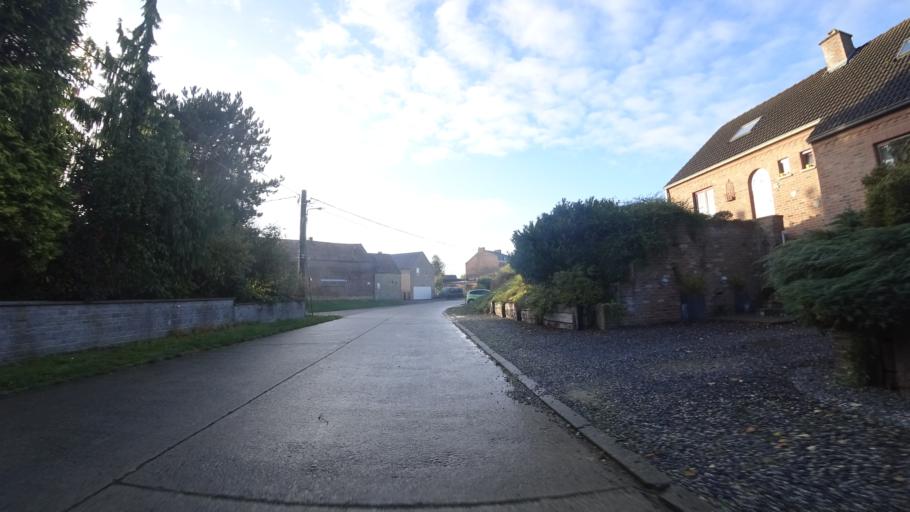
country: BE
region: Wallonia
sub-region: Province de Namur
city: Floreffe
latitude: 50.5195
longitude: 4.7807
